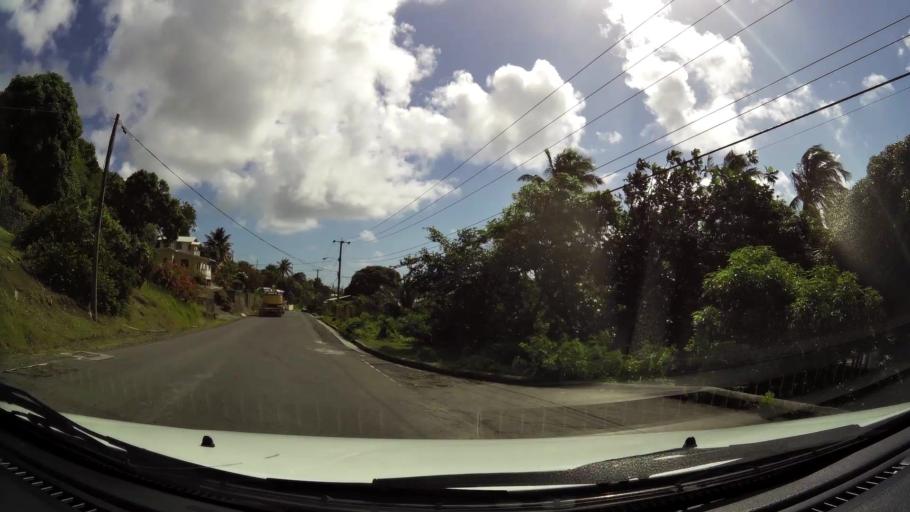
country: LC
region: Laborie Quarter
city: Laborie
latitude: 13.7533
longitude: -60.9929
